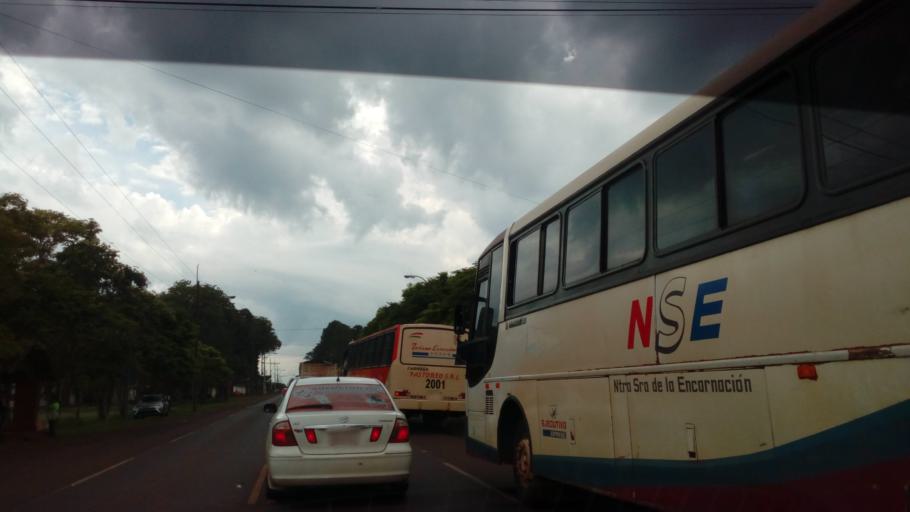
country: PY
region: Itapua
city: Obligado
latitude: -27.0825
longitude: -55.6483
